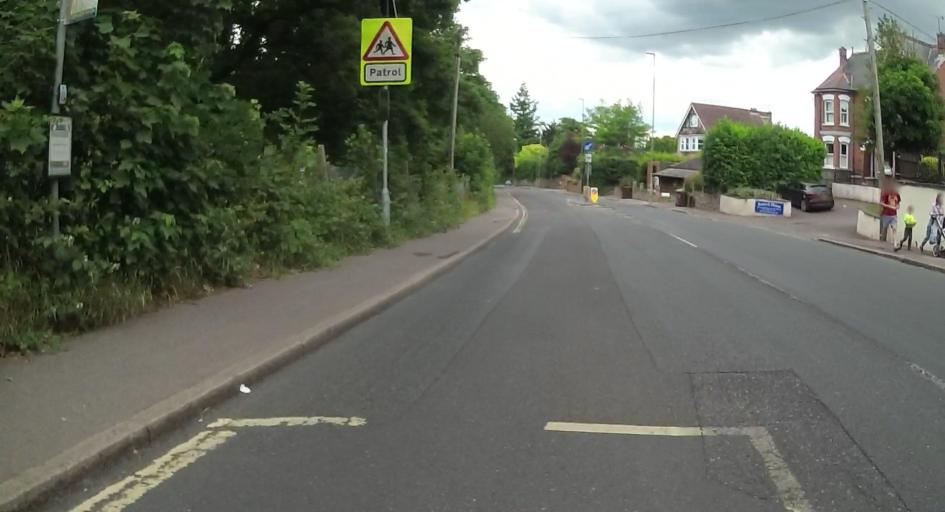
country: GB
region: England
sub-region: Hampshire
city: Aldershot
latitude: 51.2418
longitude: -0.7659
